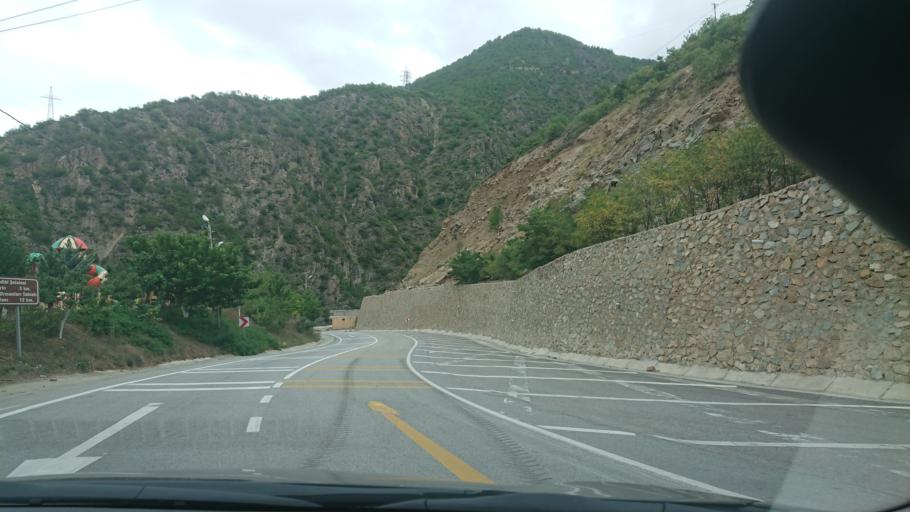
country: TR
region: Gumushane
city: Kurtun
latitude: 40.7036
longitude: 39.0801
